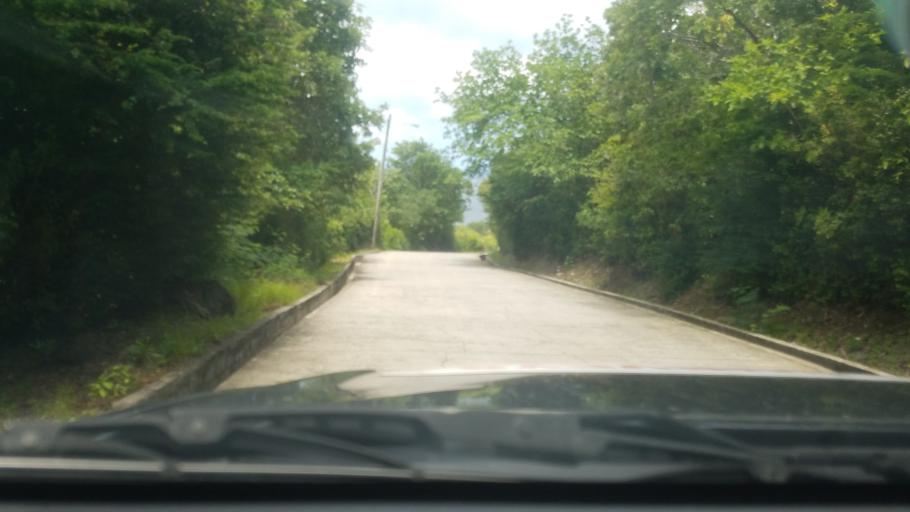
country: LC
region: Dennery Quarter
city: Dennery
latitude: 13.9199
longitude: -60.8988
